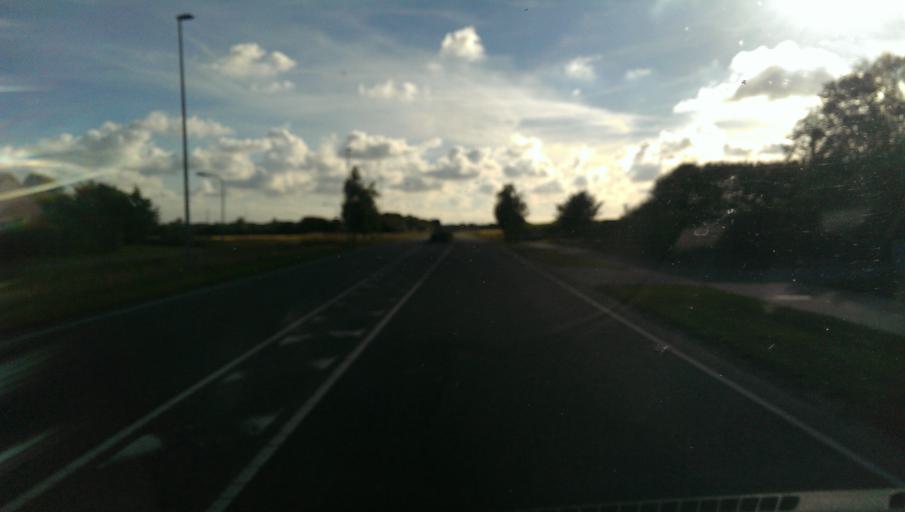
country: DK
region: South Denmark
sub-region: Esbjerg Kommune
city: Tjaereborg
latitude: 55.5074
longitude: 8.5532
